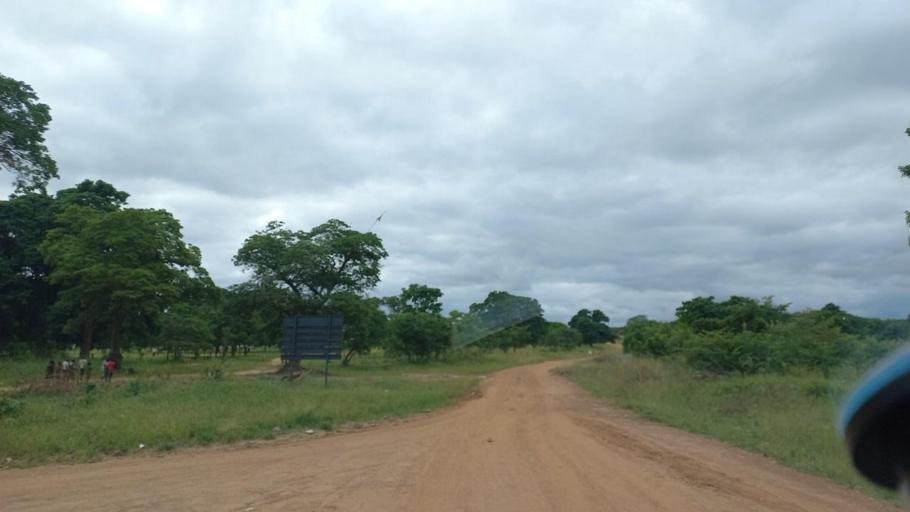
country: ZM
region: Lusaka
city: Chongwe
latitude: -15.4553
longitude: 28.8557
